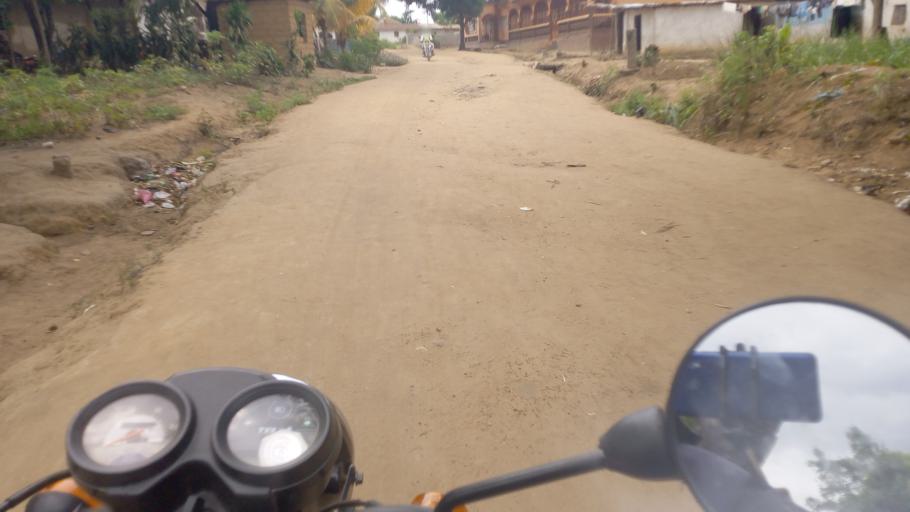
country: SL
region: Western Area
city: Waterloo
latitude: 8.3119
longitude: -13.0641
